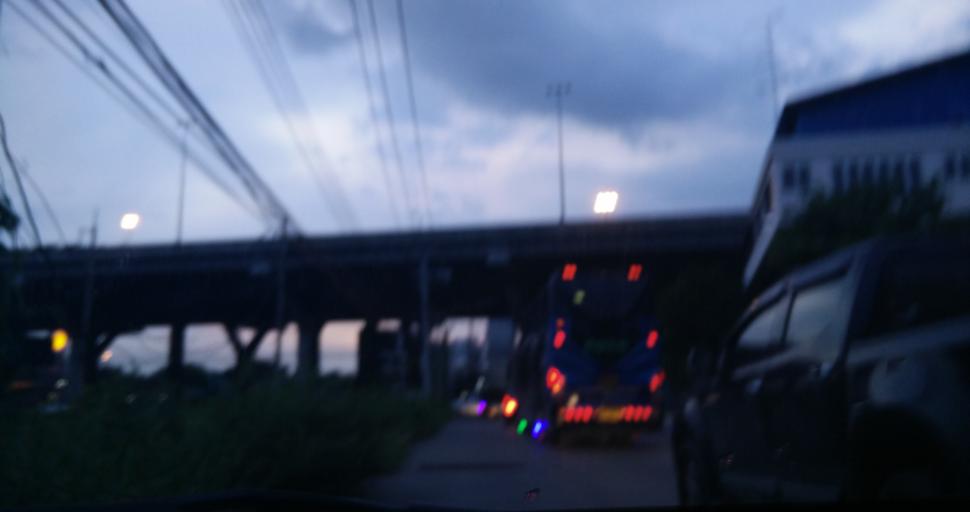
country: TH
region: Phra Nakhon Si Ayutthaya
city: Ban Bang Kadi Pathum Thani
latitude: 13.9978
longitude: 100.6158
